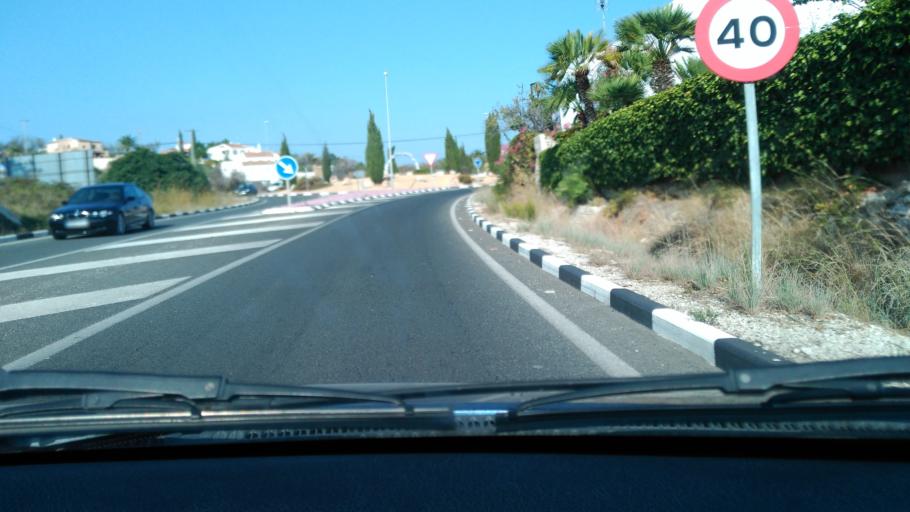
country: ES
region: Valencia
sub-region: Provincia de Alicante
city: Gata de Gorgos
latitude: 38.7843
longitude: 0.0858
